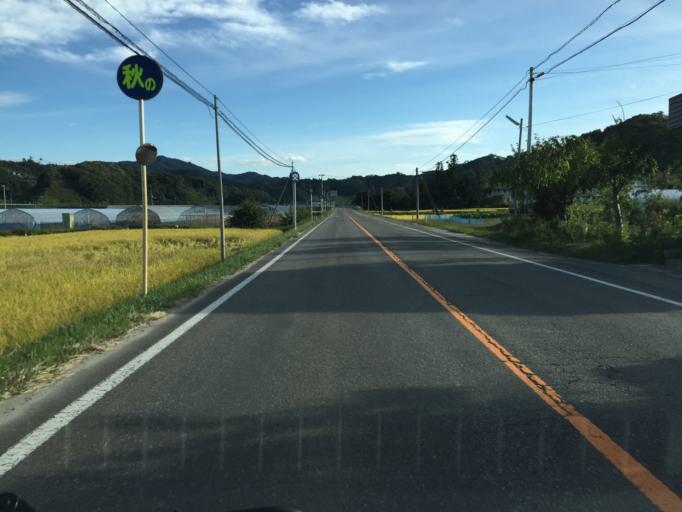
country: JP
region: Fukushima
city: Hobaramachi
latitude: 37.7530
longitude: 140.6068
